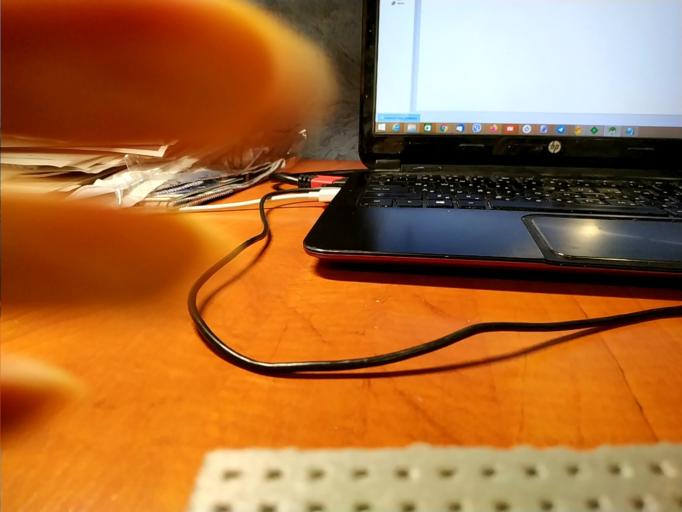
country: RU
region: Tverskaya
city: Spirovo
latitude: 57.4471
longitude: 34.9448
